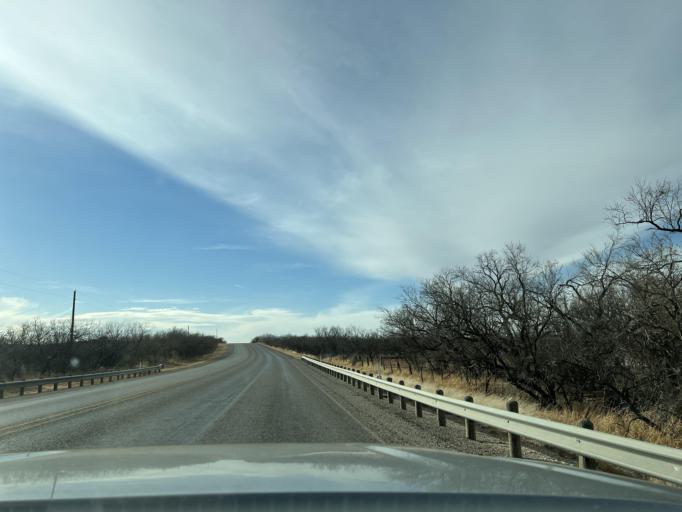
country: US
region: Texas
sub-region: Fisher County
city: Rotan
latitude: 32.7390
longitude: -100.5395
